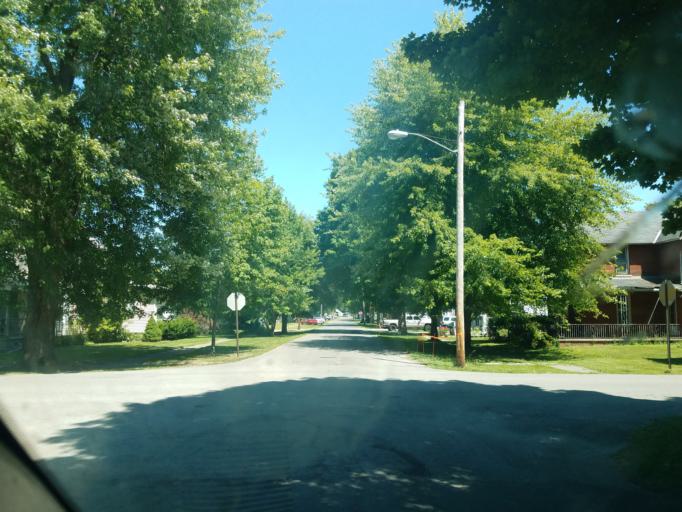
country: US
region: Ohio
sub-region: Hardin County
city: Forest
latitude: 40.7997
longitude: -83.5094
